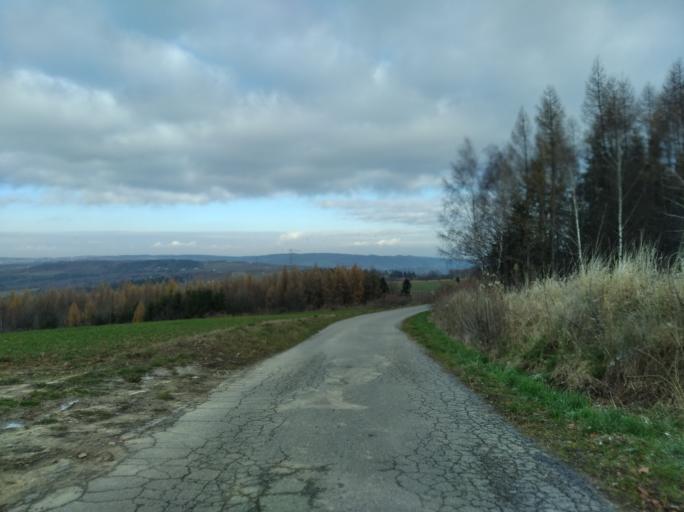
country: PL
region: Subcarpathian Voivodeship
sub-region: Powiat strzyzowski
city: Polomia
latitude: 49.8868
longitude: 21.8502
